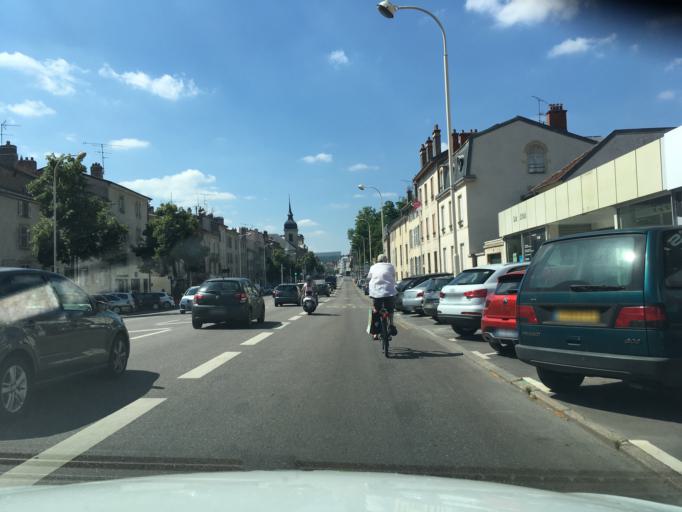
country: FR
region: Lorraine
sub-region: Departement de Meurthe-et-Moselle
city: Nancy
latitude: 48.6809
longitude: 6.1943
